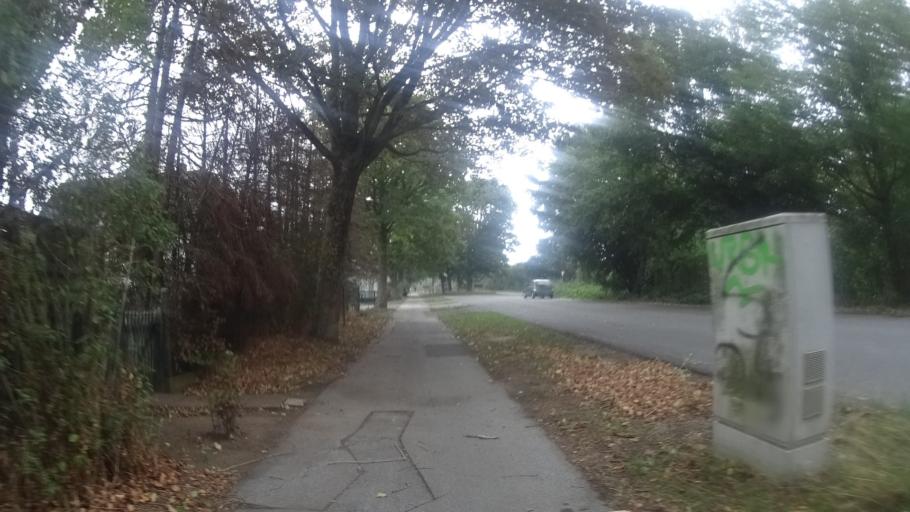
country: DE
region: North Rhine-Westphalia
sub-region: Regierungsbezirk Dusseldorf
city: Alpen
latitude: 51.5691
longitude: 6.4993
